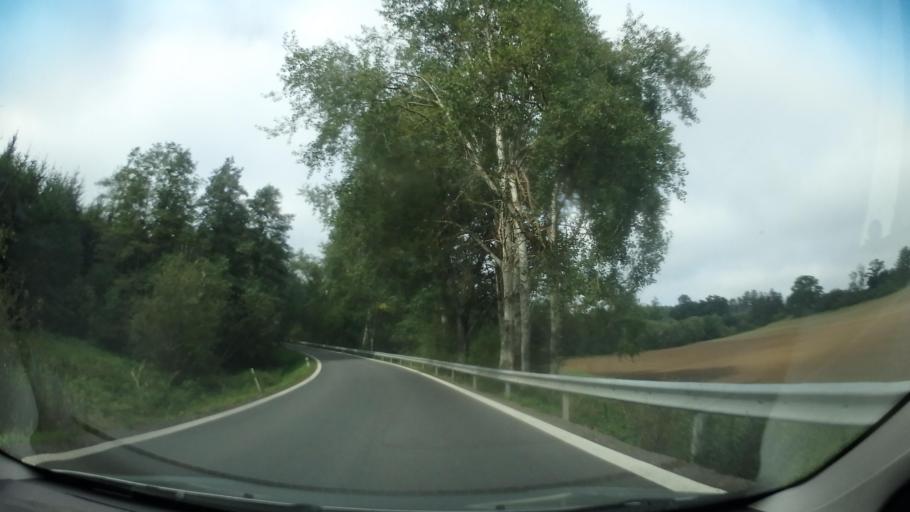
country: CZ
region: Central Bohemia
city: Neveklov
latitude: 49.7537
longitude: 14.5760
